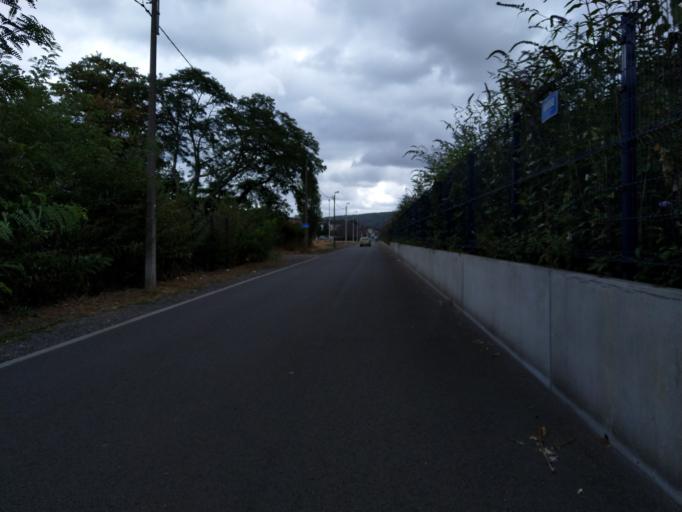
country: BE
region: Wallonia
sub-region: Province de Liege
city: Saint-Nicolas
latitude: 50.6142
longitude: 5.5456
